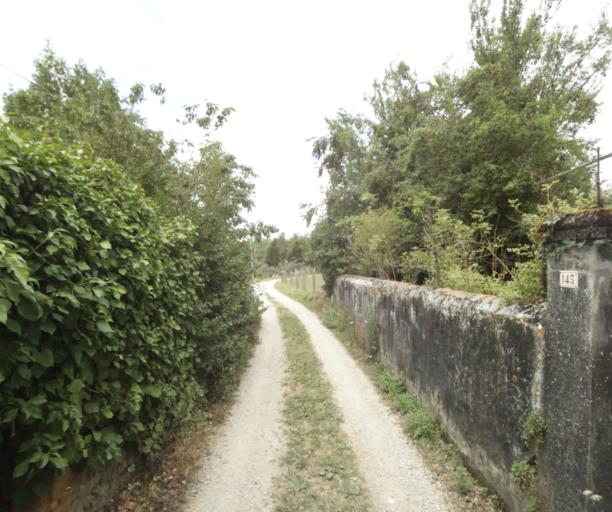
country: FR
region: Midi-Pyrenees
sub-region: Departement du Tarn
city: Soreze
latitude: 43.4493
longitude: 2.0670
